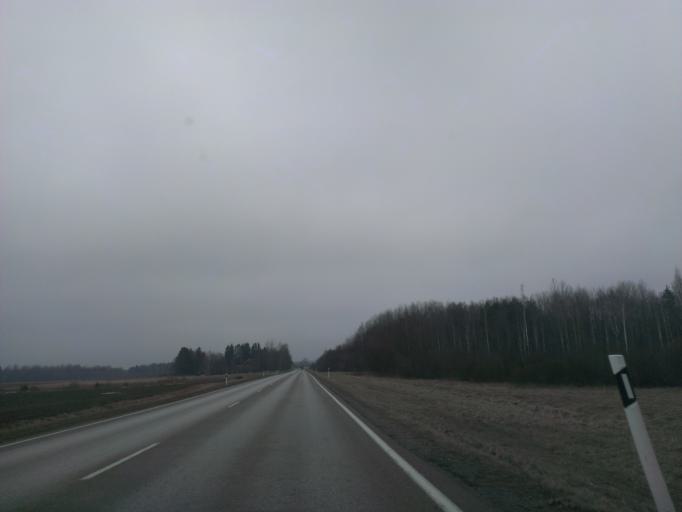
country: EE
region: Paernumaa
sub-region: Audru vald
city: Audru
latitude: 58.4388
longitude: 24.2529
